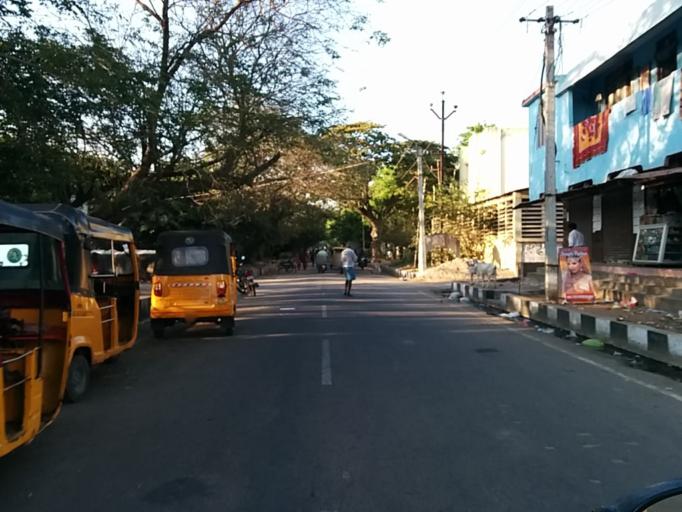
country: IN
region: Pondicherry
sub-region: Puducherry
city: Puducherry
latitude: 11.9215
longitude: 79.8304
